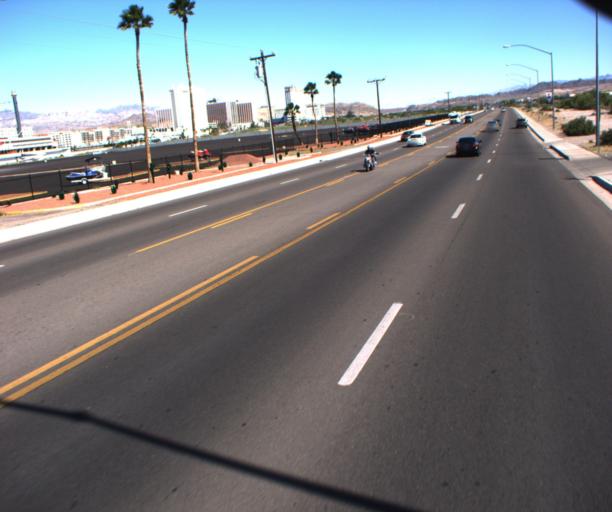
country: US
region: Arizona
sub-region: Mohave County
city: Bullhead City
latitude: 35.1536
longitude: -114.5673
